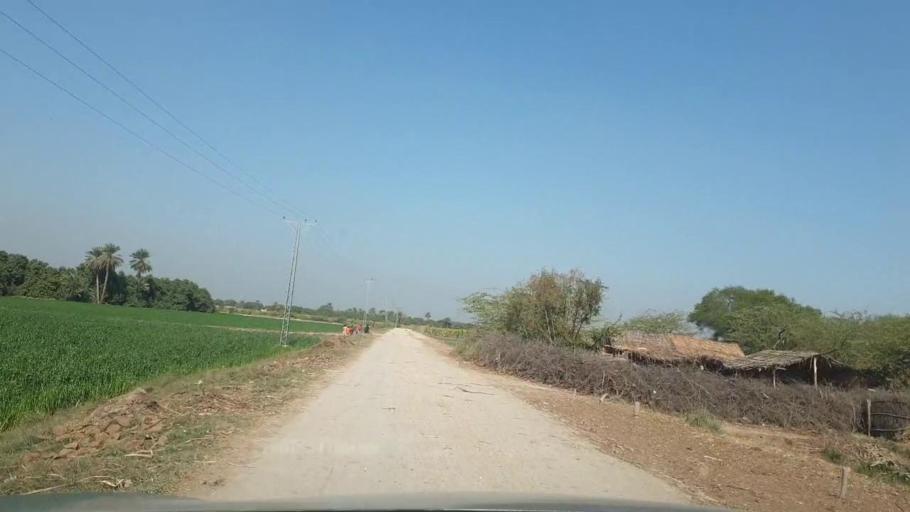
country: PK
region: Sindh
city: Tando Adam
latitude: 25.6320
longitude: 68.6491
